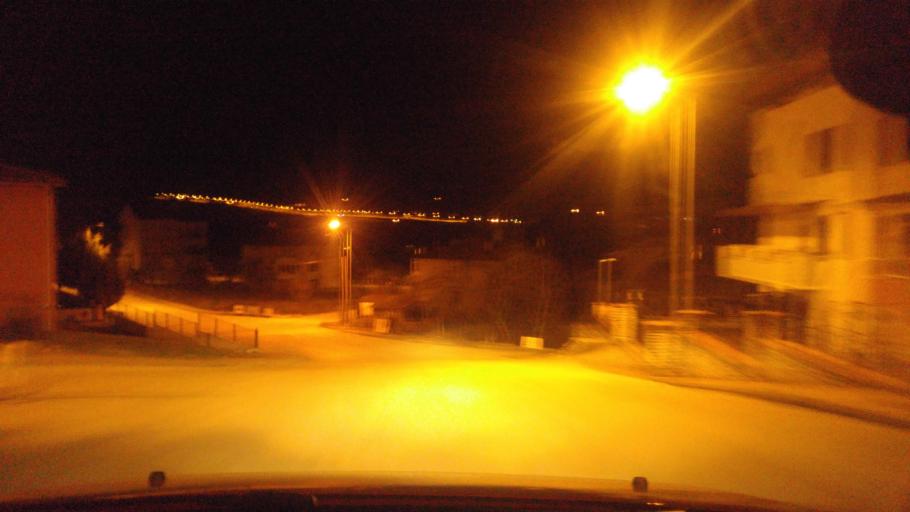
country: TR
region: Karabuk
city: Safranbolu
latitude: 41.2654
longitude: 32.6794
